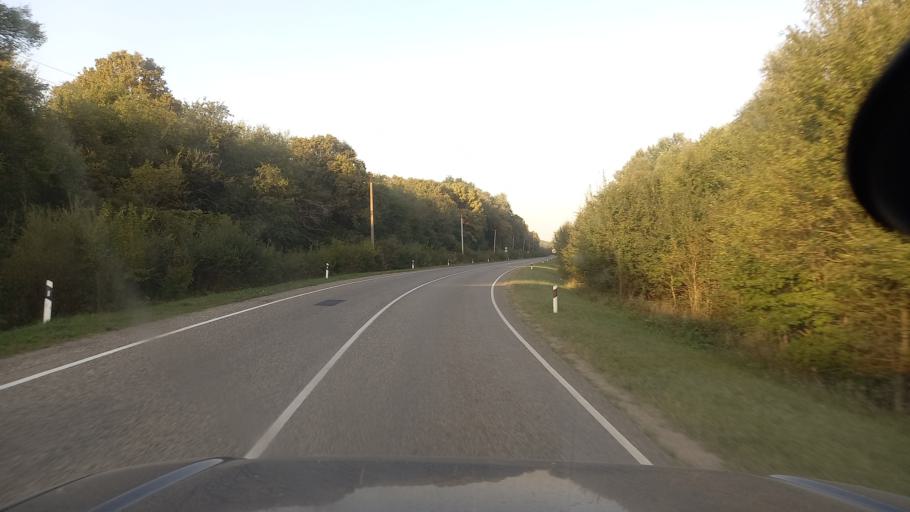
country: RU
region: Krasnodarskiy
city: Smolenskaya
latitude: 44.7330
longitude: 38.7180
